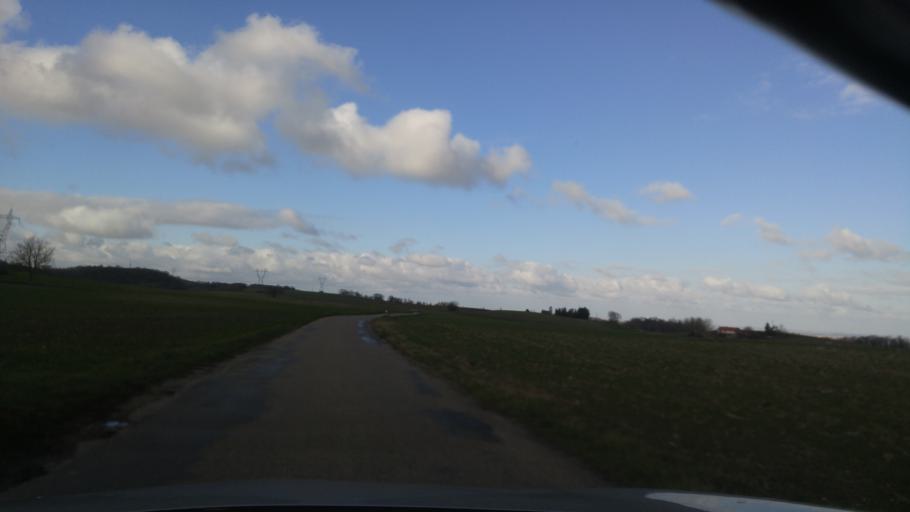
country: FR
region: Rhone-Alpes
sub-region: Departement de l'Isere
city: Roche
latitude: 45.5749
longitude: 5.1787
